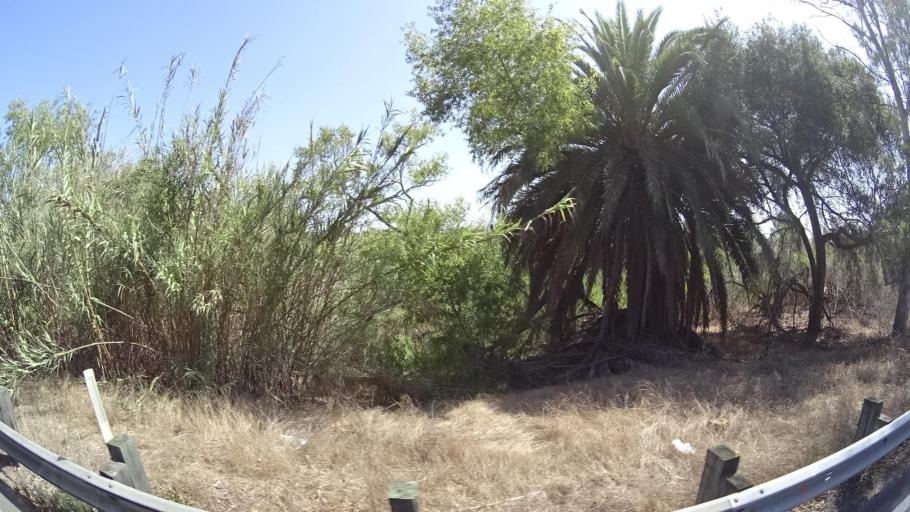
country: US
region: California
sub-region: San Diego County
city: Fairbanks Ranch
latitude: 33.0004
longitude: -117.2064
